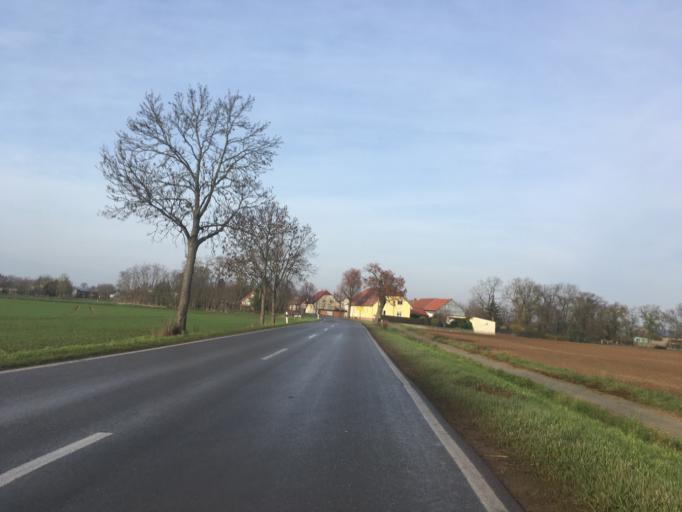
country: DE
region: Brandenburg
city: Wriezen
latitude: 52.7724
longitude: 14.1559
